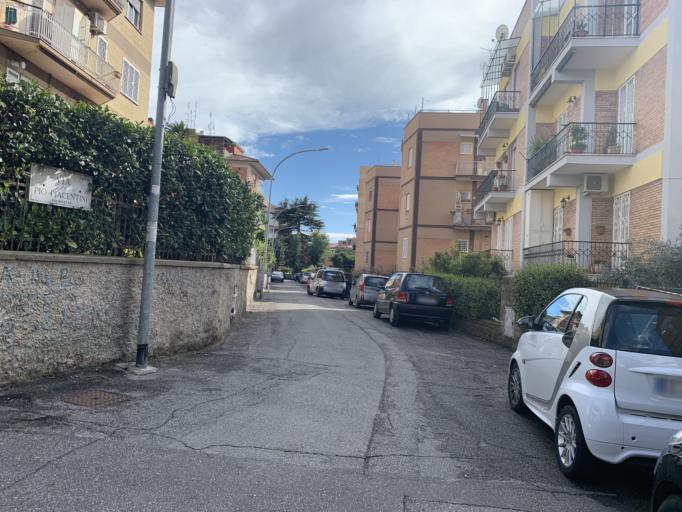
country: VA
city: Vatican City
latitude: 41.8808
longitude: 12.4183
